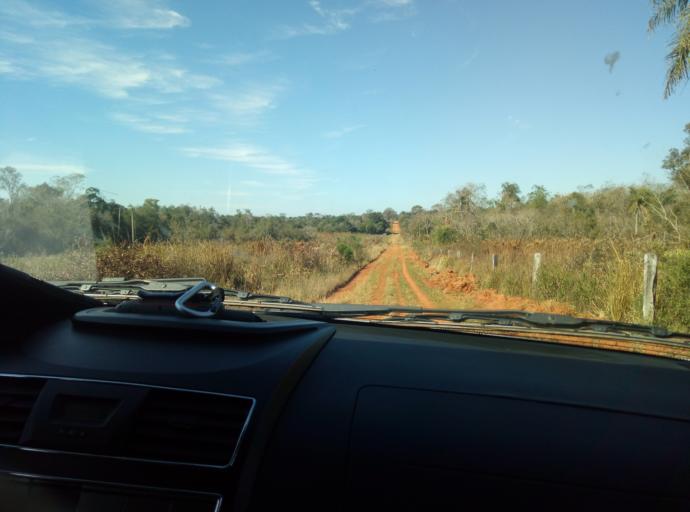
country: PY
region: Caaguazu
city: Carayao
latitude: -25.1685
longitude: -56.3101
